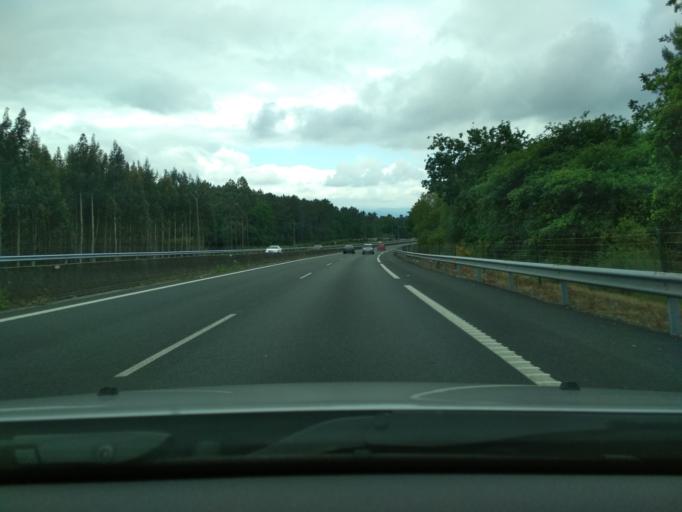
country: ES
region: Galicia
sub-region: Provincia da Coruna
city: Santiago de Compostela
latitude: 42.8246
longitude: -8.5708
